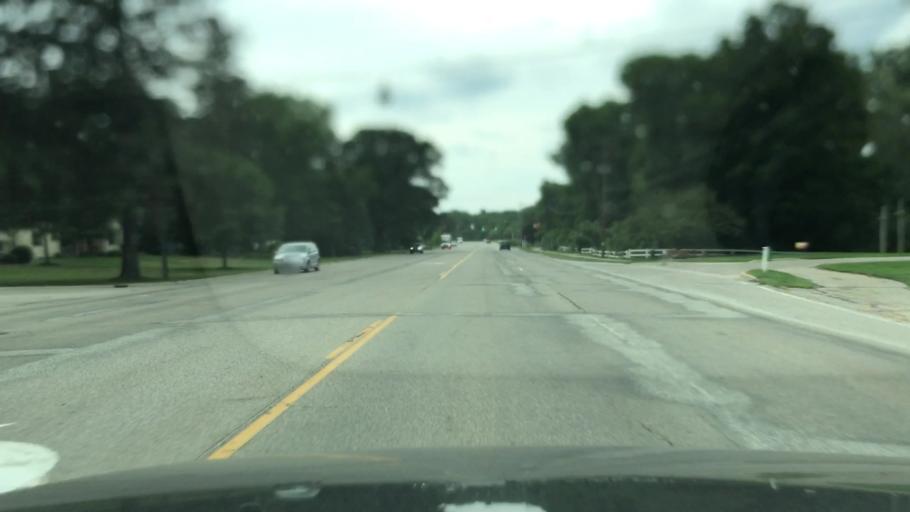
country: US
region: Michigan
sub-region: Kent County
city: Forest Hills
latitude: 42.9186
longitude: -85.5035
